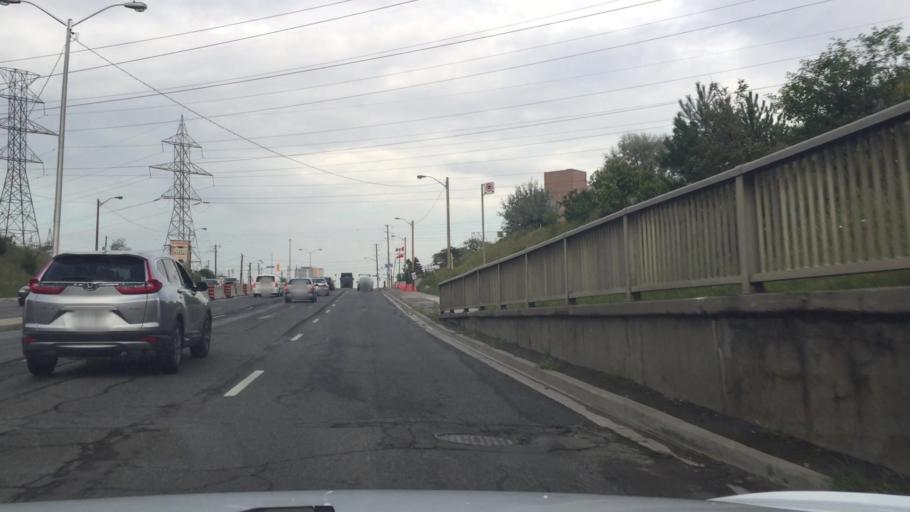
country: CA
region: Ontario
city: Concord
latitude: 43.7526
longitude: -79.5392
